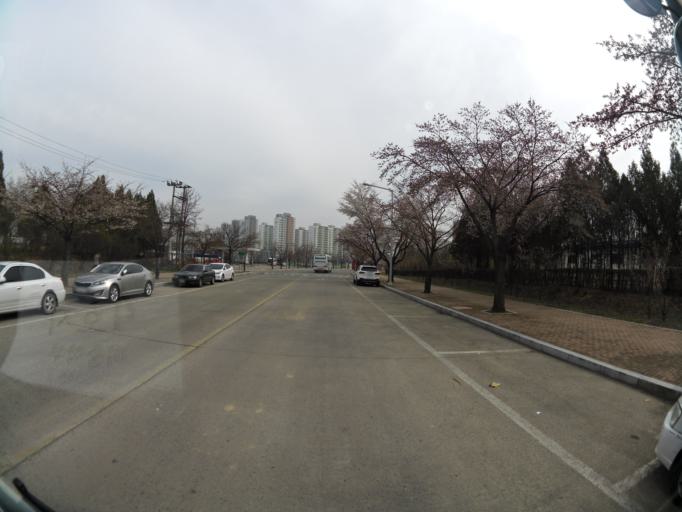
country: KR
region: Gyeongsangbuk-do
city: Gyeongsan-si
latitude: 35.8356
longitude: 128.7633
